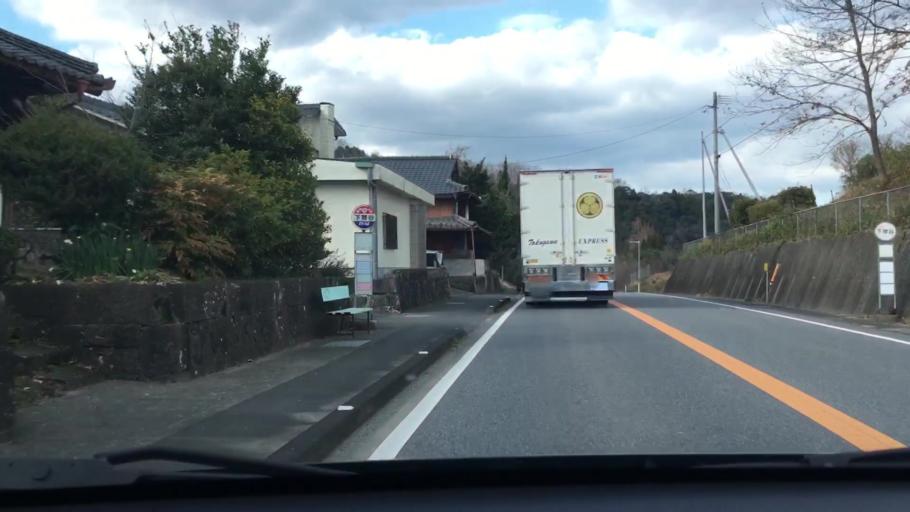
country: JP
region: Oita
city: Usuki
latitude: 33.0206
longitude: 131.6976
